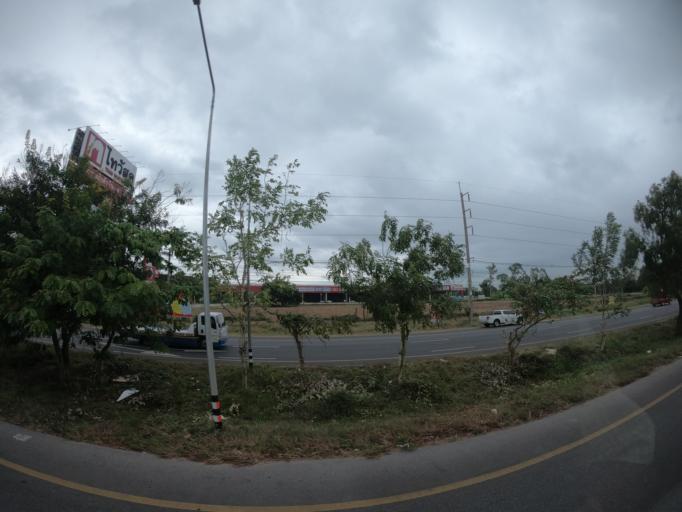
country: TH
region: Roi Et
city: Roi Et
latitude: 16.0561
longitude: 103.6199
